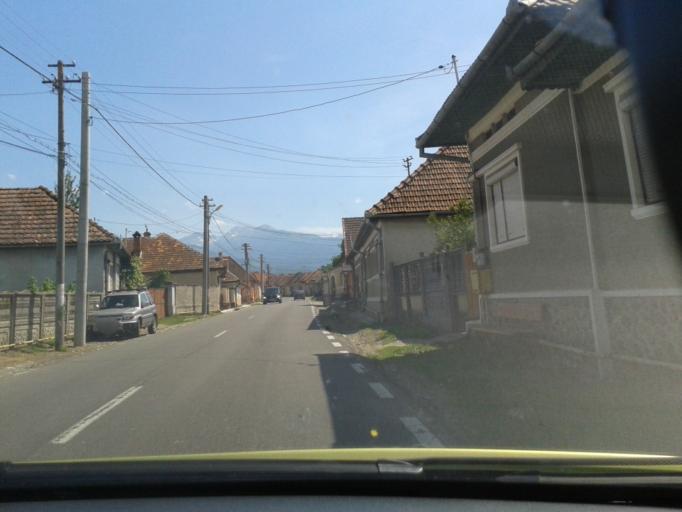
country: RO
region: Sibiu
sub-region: Comuna Cartisoara
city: Cartisoara
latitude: 45.7310
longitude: 24.5743
